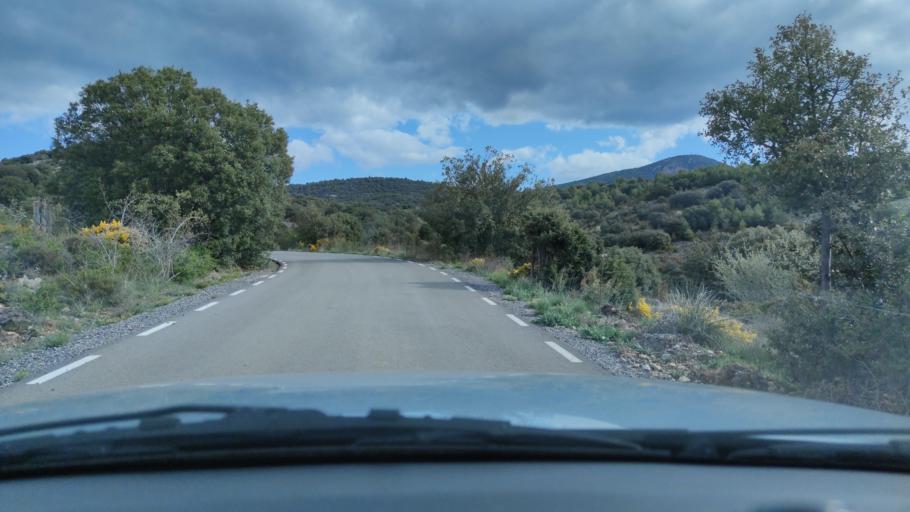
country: ES
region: Catalonia
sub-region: Provincia de Lleida
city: Coll de Nargo
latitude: 42.2321
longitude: 1.4040
